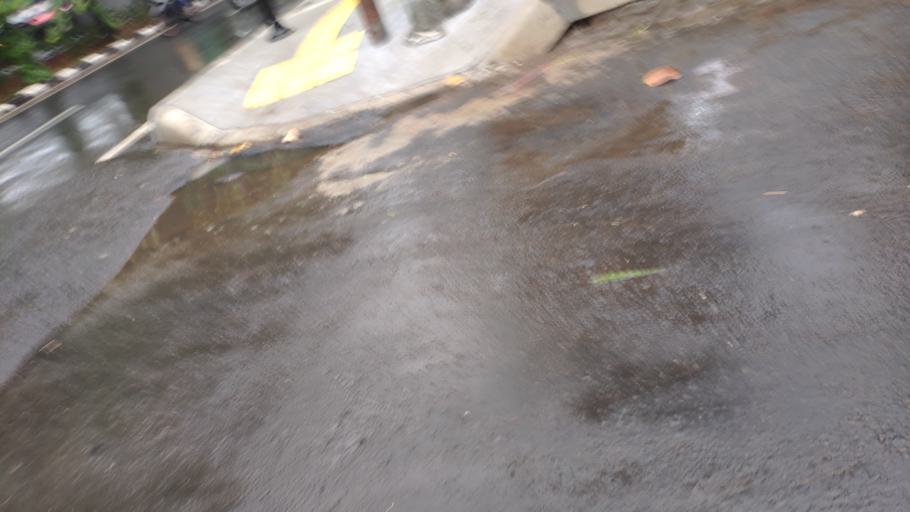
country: ID
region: Jakarta Raya
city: Jakarta
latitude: -6.2066
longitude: 106.8735
